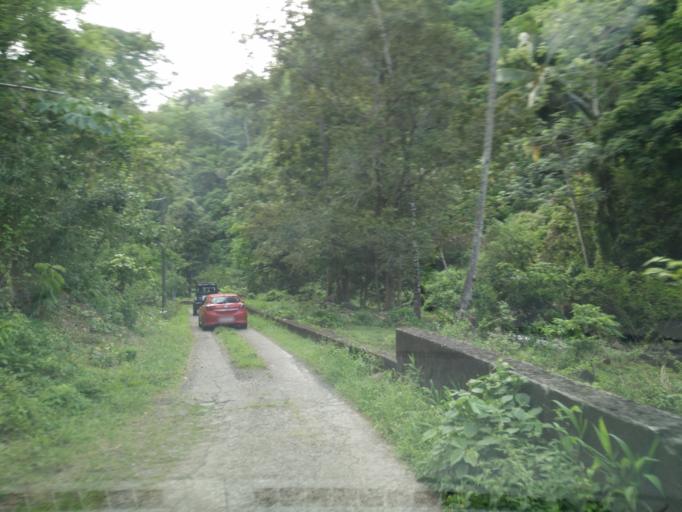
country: MQ
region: Martinique
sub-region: Martinique
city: Saint-Pierre
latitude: 14.7184
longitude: -61.1600
